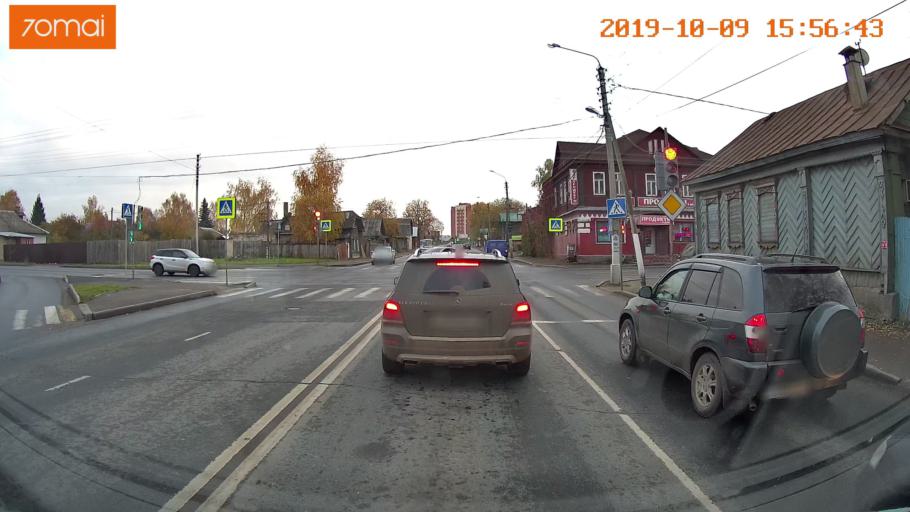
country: RU
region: Kostroma
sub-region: Kostromskoy Rayon
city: Kostroma
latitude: 57.7739
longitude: 40.9467
